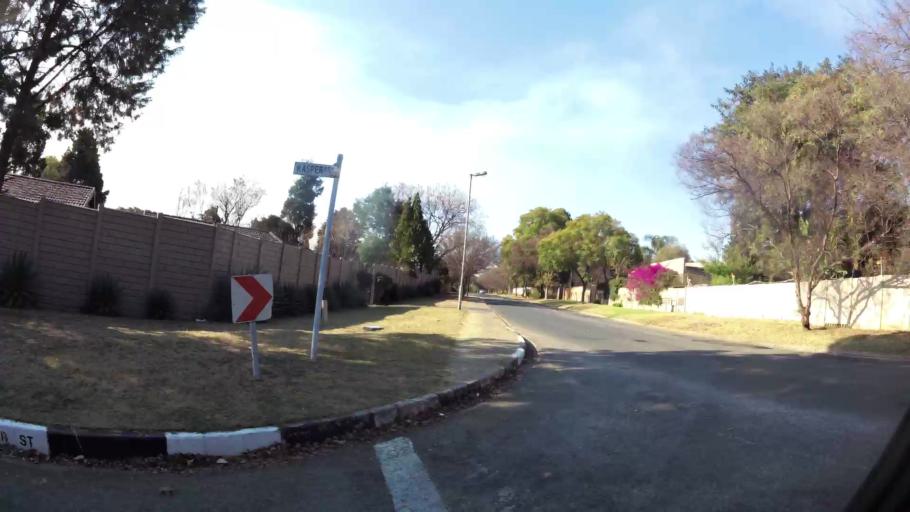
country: ZA
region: Gauteng
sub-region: City of Johannesburg Metropolitan Municipality
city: Roodepoort
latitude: -26.0965
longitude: 27.9738
